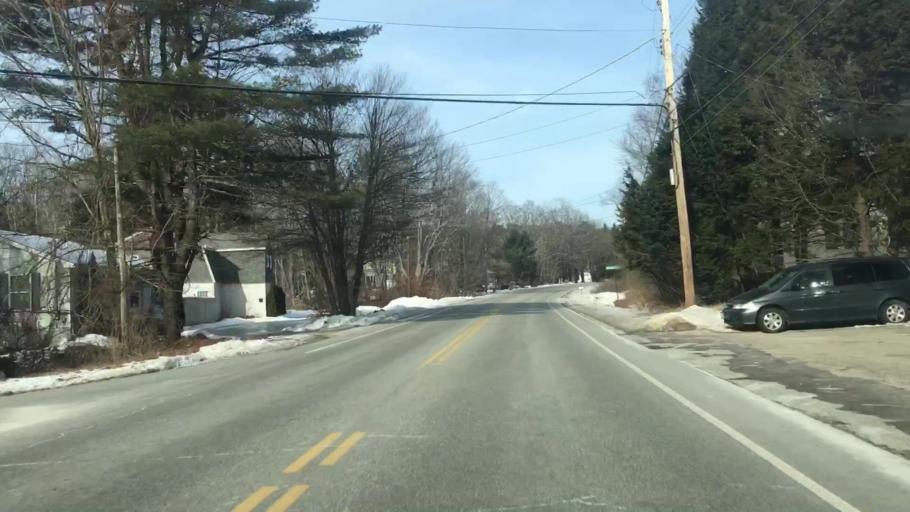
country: US
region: Maine
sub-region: Cumberland County
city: South Windham
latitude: 43.7561
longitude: -70.4250
